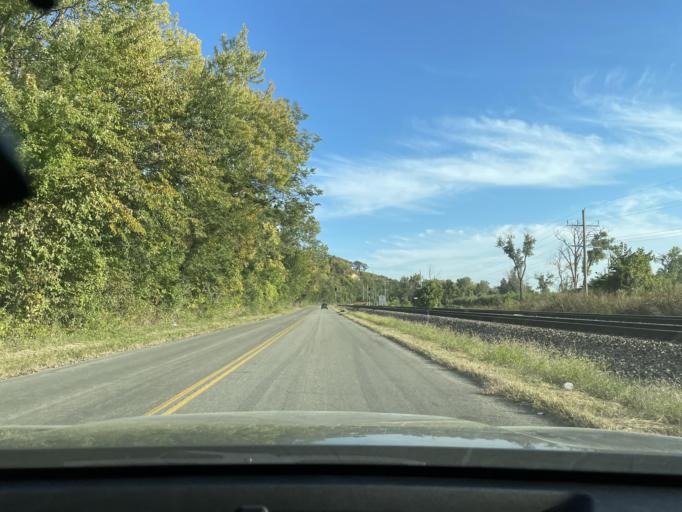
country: US
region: Kansas
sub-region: Doniphan County
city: Elwood
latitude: 39.7763
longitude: -94.8685
